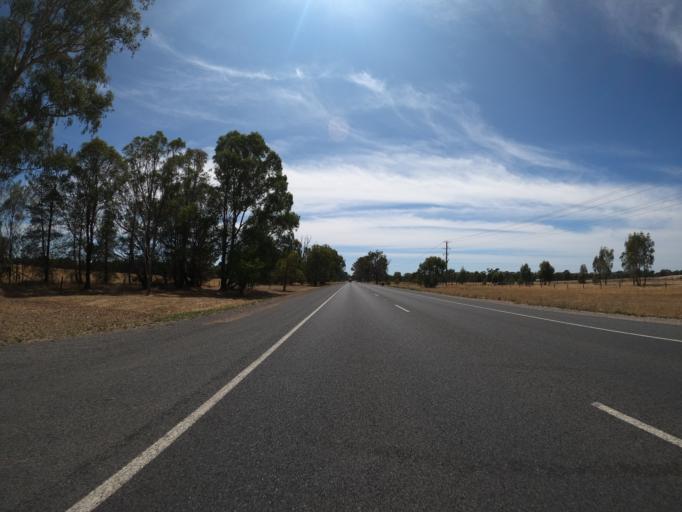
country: AU
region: Victoria
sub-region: Benalla
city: Benalla
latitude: -36.5259
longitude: 146.0512
